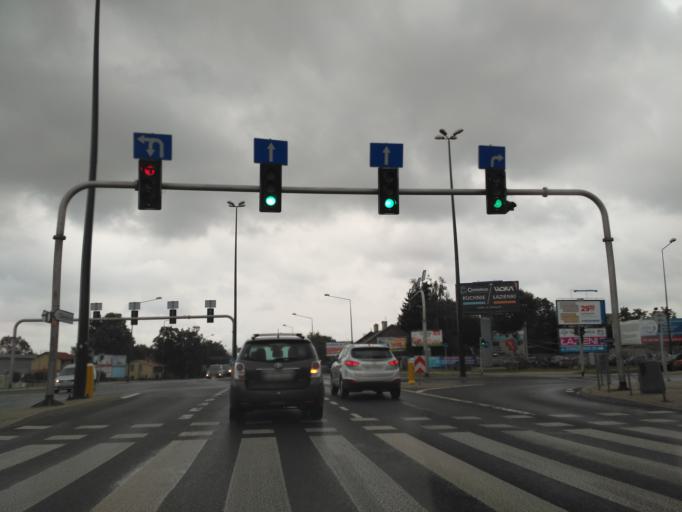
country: PL
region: Lublin Voivodeship
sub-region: Powiat lubelski
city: Lublin
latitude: 51.2700
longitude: 22.5731
